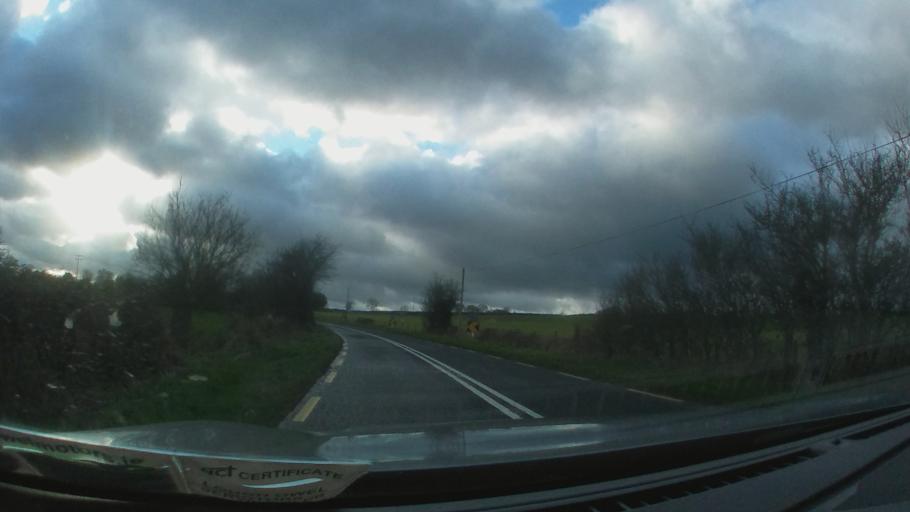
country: IE
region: Leinster
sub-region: Kilkenny
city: Thomastown
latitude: 52.5607
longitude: -7.1220
